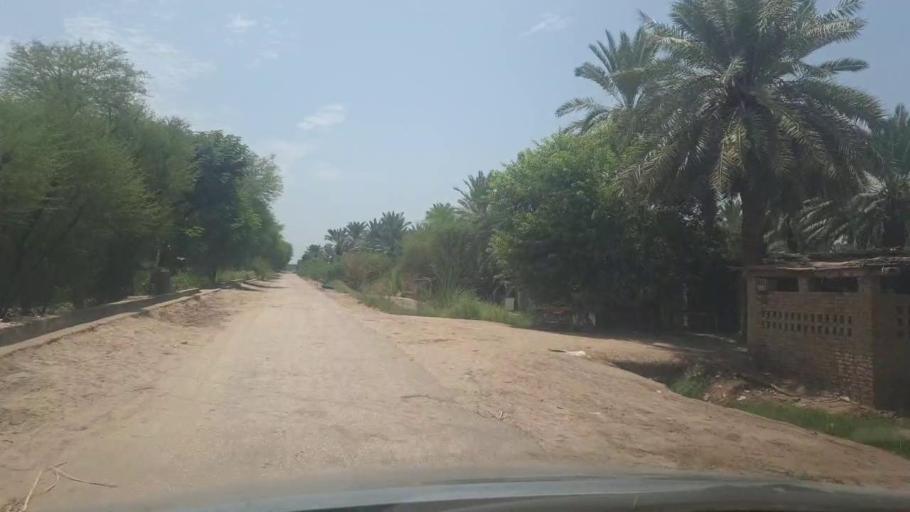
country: PK
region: Sindh
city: Kot Diji
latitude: 27.3989
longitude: 68.7174
